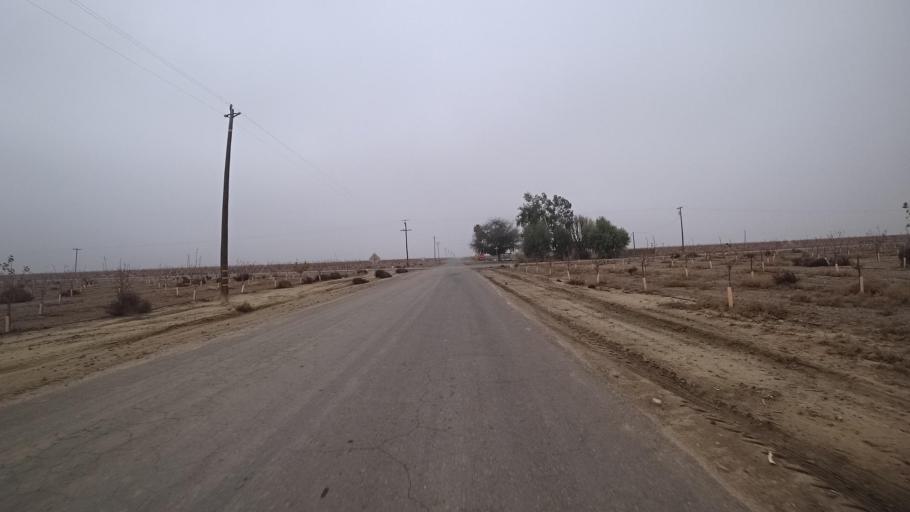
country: US
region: California
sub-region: Kern County
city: Wasco
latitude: 35.7039
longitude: -119.4194
